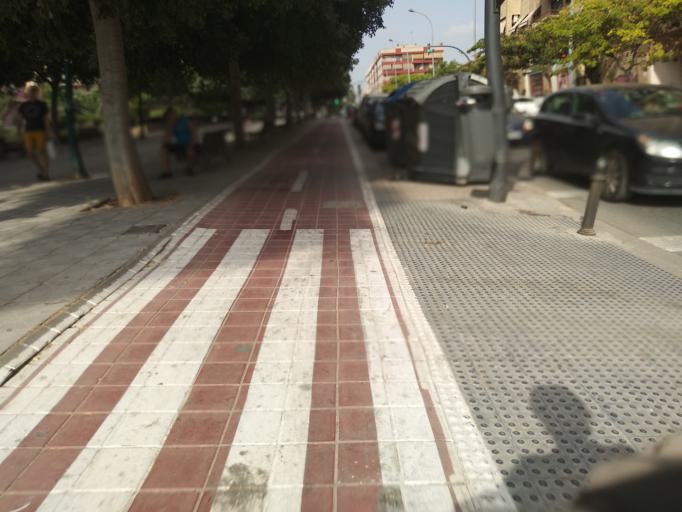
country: ES
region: Valencia
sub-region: Provincia de Valencia
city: Tavernes Blanques
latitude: 39.4894
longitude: -0.3783
